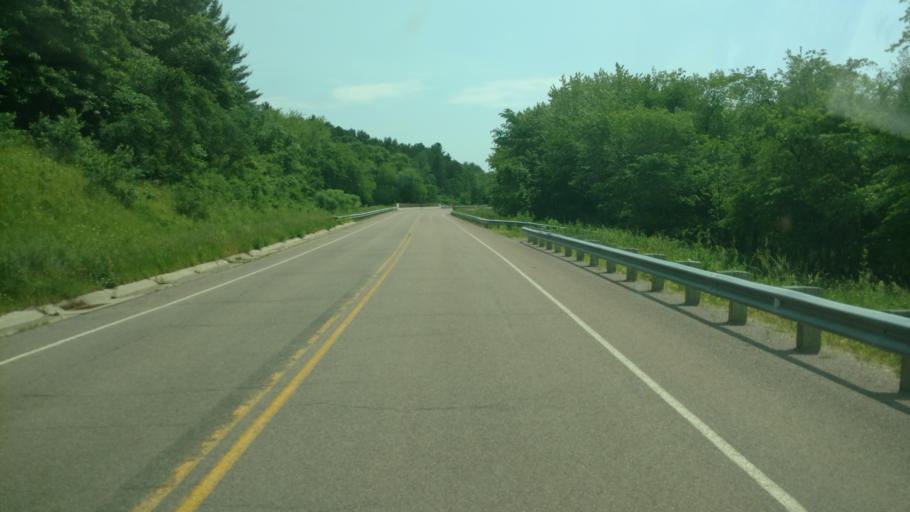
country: US
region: Wisconsin
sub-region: Monroe County
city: Cashton
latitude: 43.6601
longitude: -90.5920
